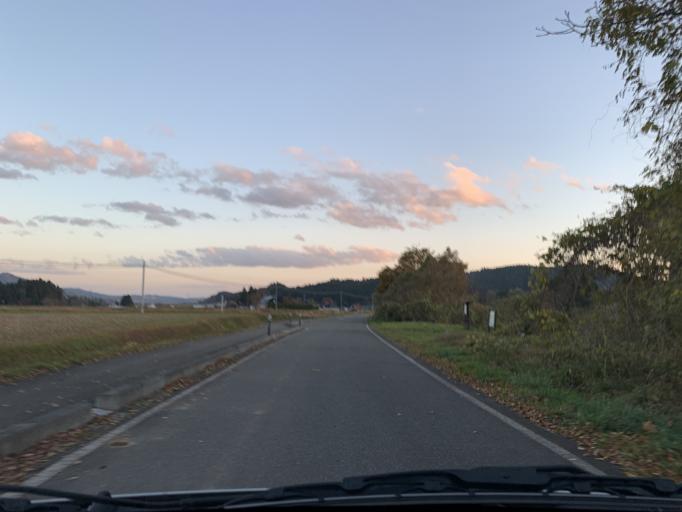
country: JP
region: Iwate
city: Ichinoseki
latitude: 39.0143
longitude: 141.0946
